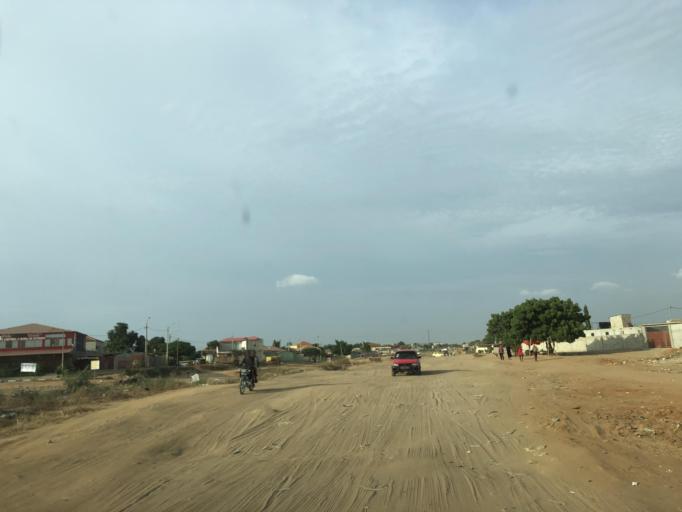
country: AO
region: Luanda
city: Luanda
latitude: -8.9223
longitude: 13.3075
